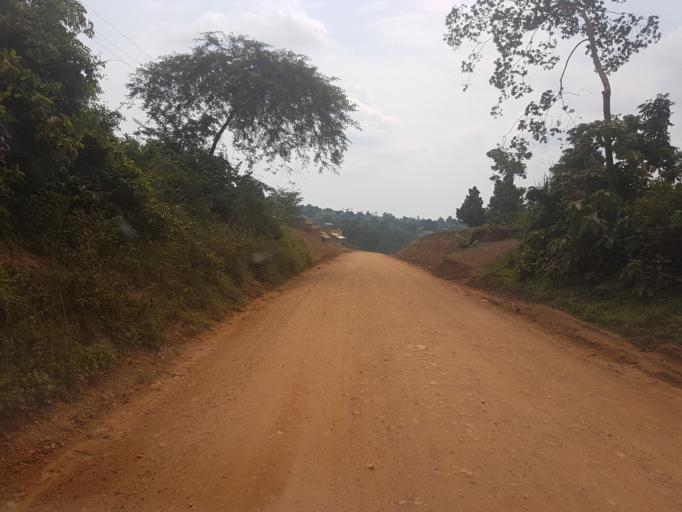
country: UG
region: Western Region
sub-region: Kanungu District
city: Ntungamo
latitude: -0.8212
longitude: 29.7085
